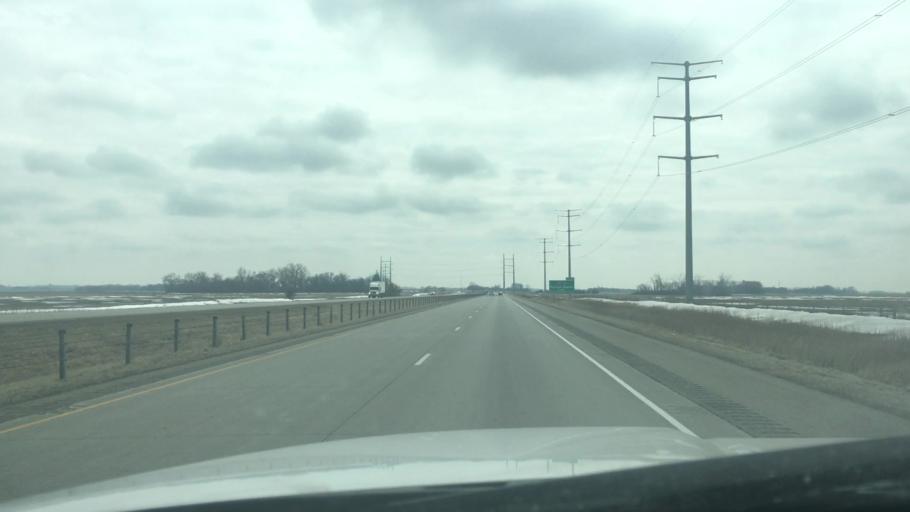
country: US
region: Minnesota
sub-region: Clay County
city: Barnesville
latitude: 46.5775
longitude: -96.3285
